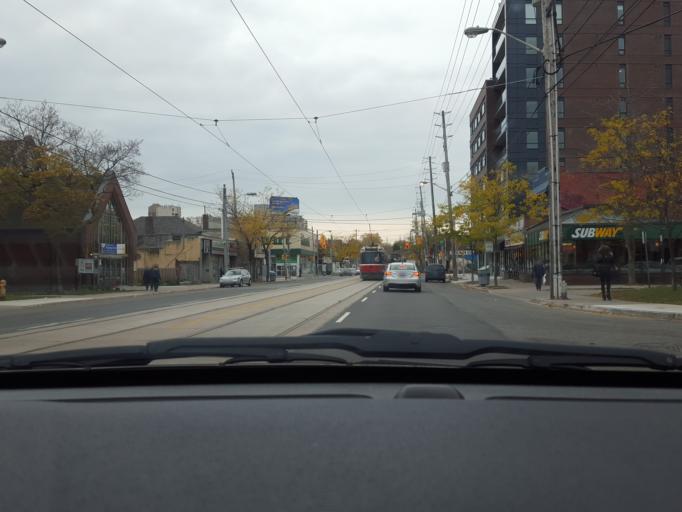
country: CA
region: Ontario
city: Etobicoke
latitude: 43.6158
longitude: -79.4882
